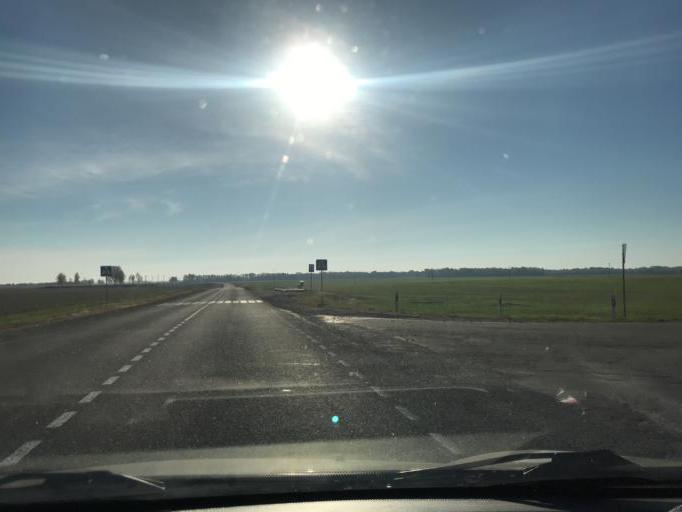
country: BY
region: Gomel
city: Brahin
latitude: 51.8058
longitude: 30.1154
